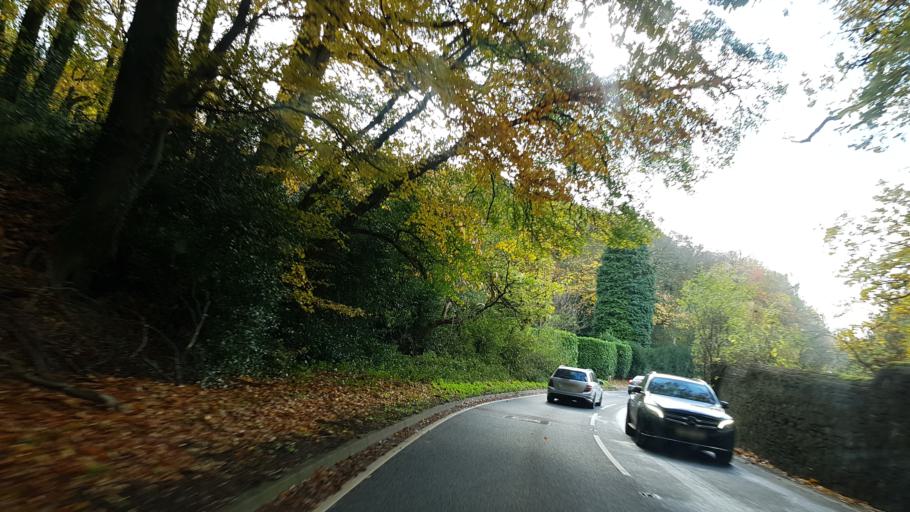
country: GB
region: England
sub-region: Surrey
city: Milford
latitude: 51.1383
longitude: -0.6727
